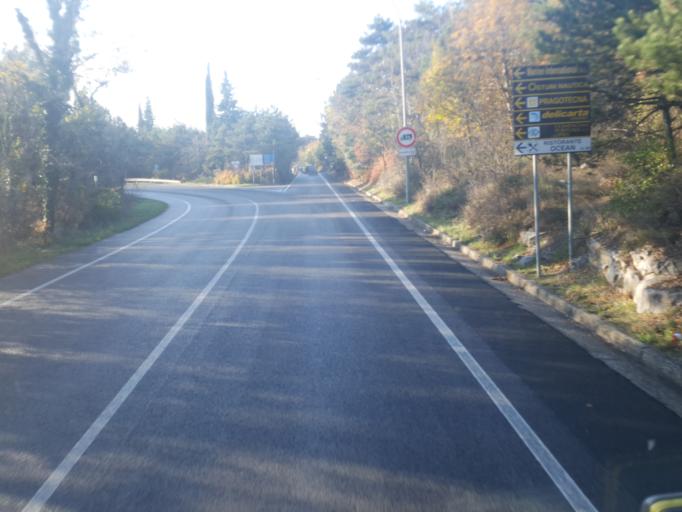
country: IT
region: Friuli Venezia Giulia
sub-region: Provincia di Gorizia
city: Monfalcone
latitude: 45.8015
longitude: 13.5694
